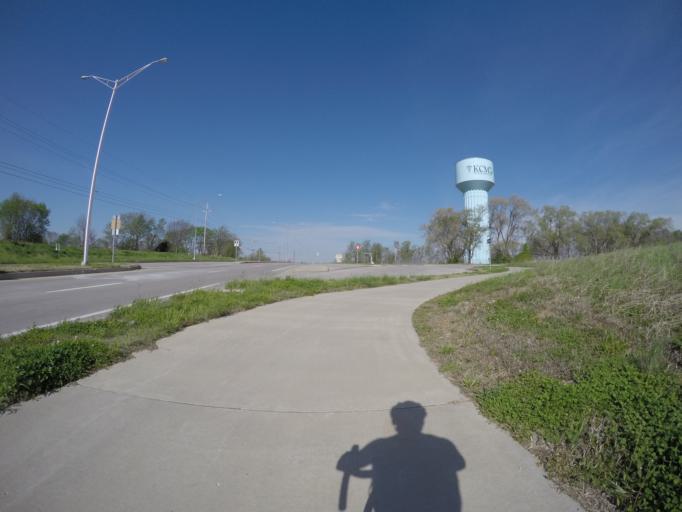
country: US
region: Missouri
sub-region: Cass County
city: Raymore
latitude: 38.8542
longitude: -94.4301
